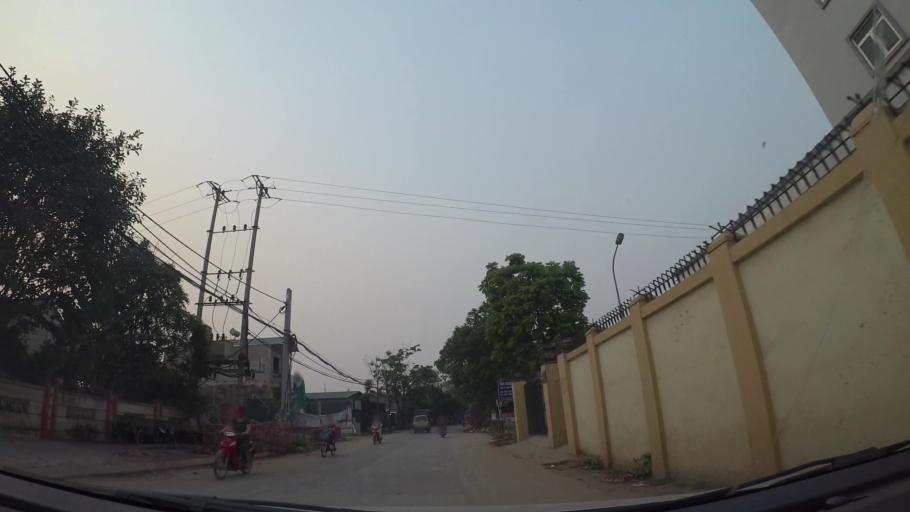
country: VN
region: Ha Noi
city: Ha Dong
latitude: 20.9949
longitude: 105.7245
